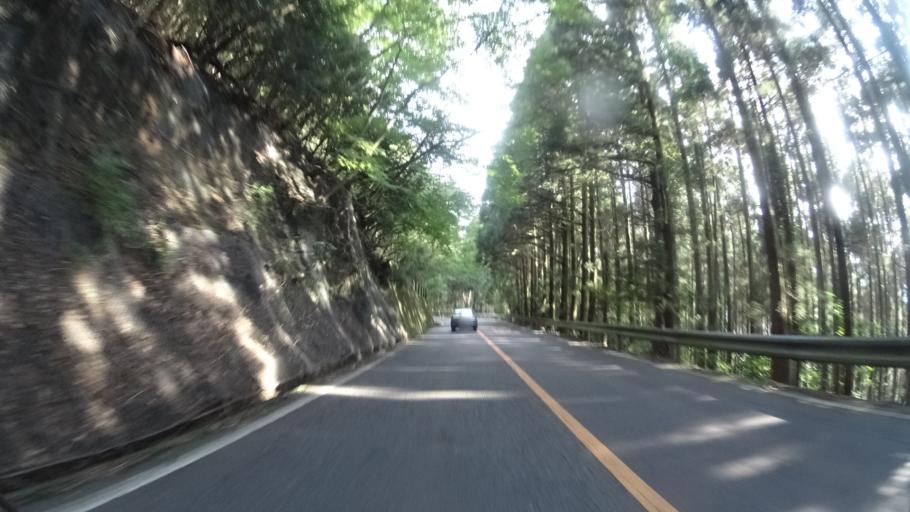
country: JP
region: Oita
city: Beppu
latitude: 33.2660
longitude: 131.3706
